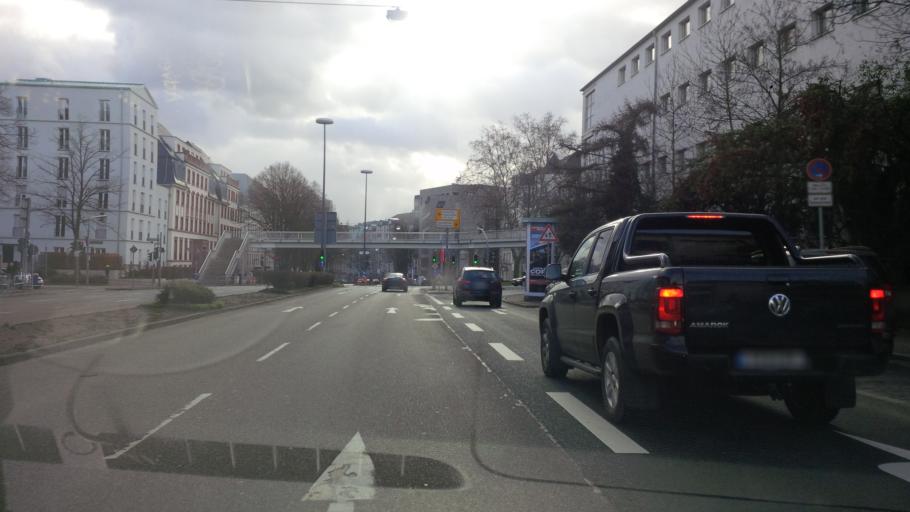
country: DE
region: Hesse
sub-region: Regierungsbezirk Darmstadt
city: Frankfurt am Main
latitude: 50.1288
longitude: 8.6726
